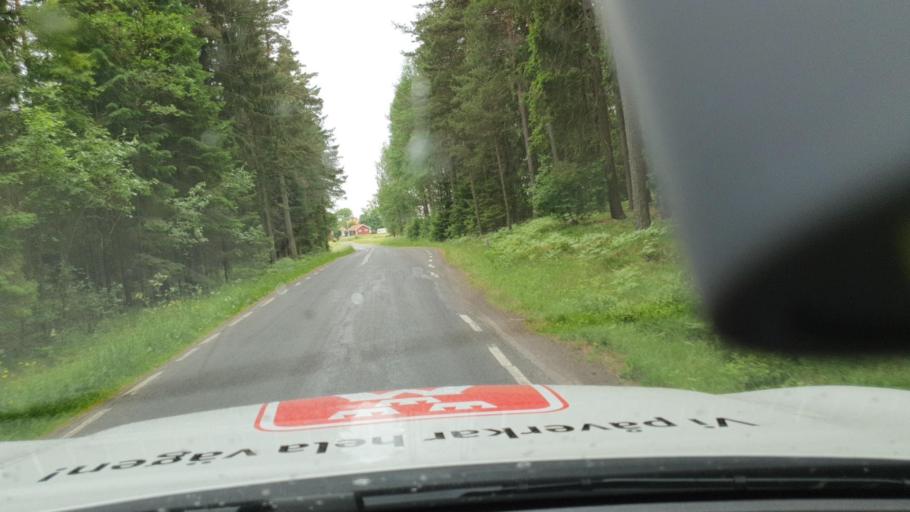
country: SE
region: Vaestra Goetaland
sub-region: Tibro Kommun
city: Tibro
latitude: 58.3309
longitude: 14.1901
